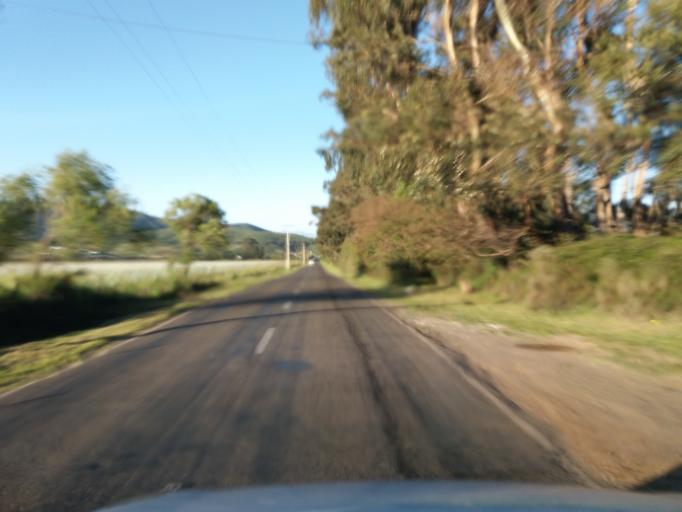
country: CL
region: Valparaiso
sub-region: Provincia de Quillota
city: Quillota
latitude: -32.9054
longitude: -71.3051
